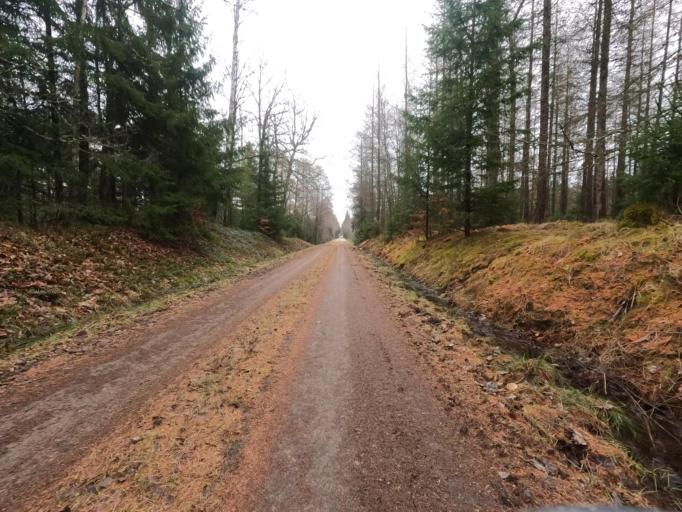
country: SE
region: Kronoberg
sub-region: Markaryds Kommun
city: Stromsnasbruk
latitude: 56.7886
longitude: 13.6340
